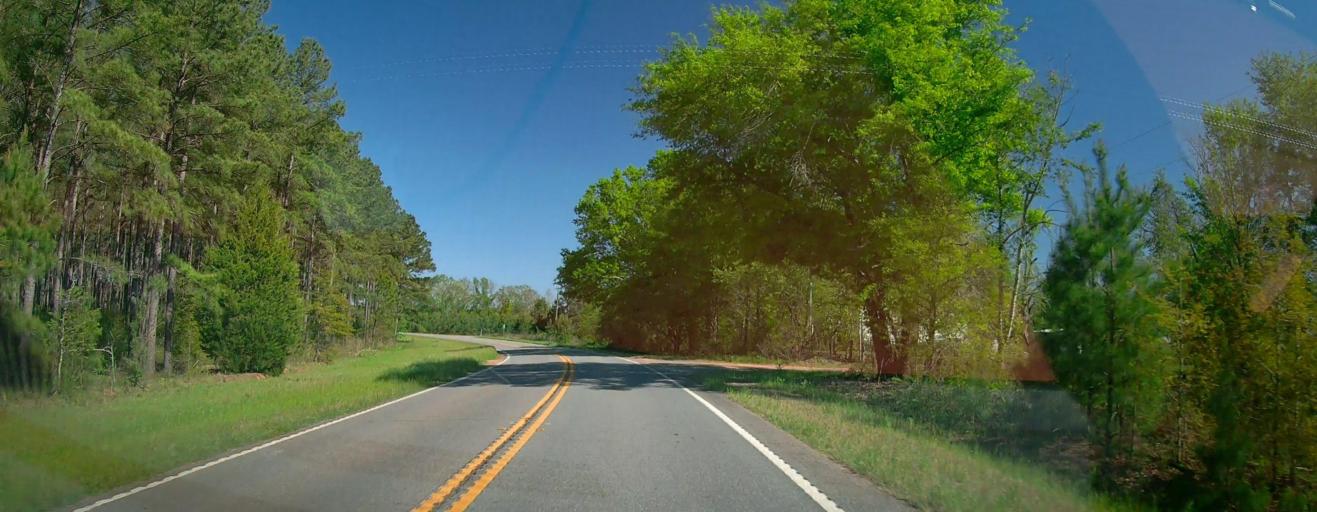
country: US
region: Georgia
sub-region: Dooly County
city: Unadilla
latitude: 32.2562
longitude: -83.6474
